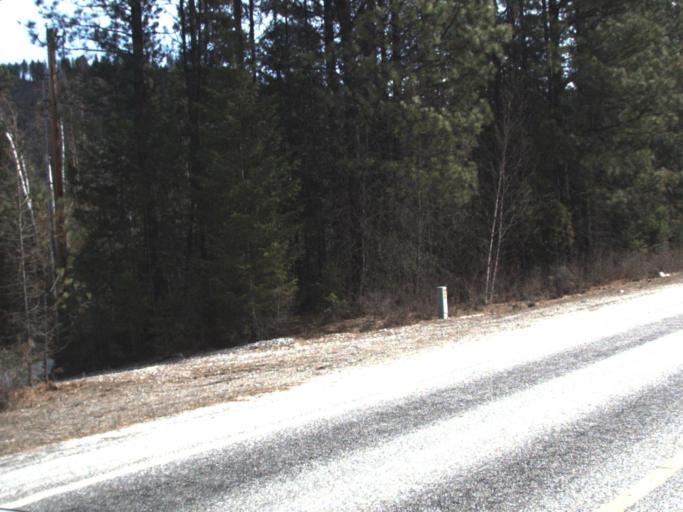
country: US
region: Washington
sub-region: Stevens County
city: Chewelah
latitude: 48.5506
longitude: -117.3358
